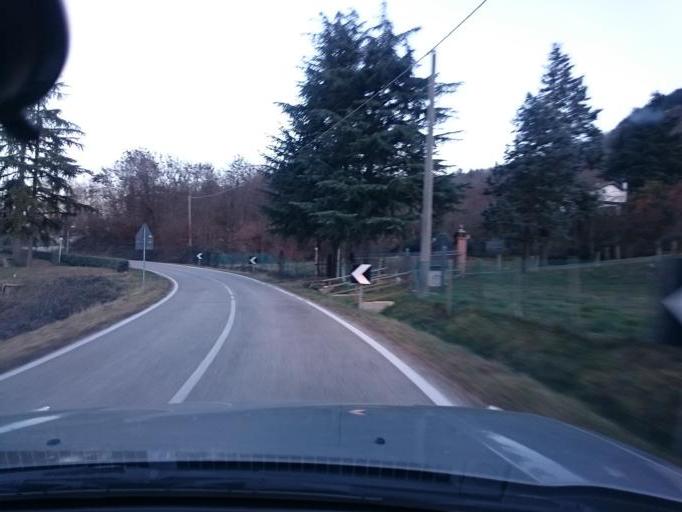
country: IT
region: Veneto
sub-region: Provincia di Padova
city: Galzignano
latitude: 45.3240
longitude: 11.7046
